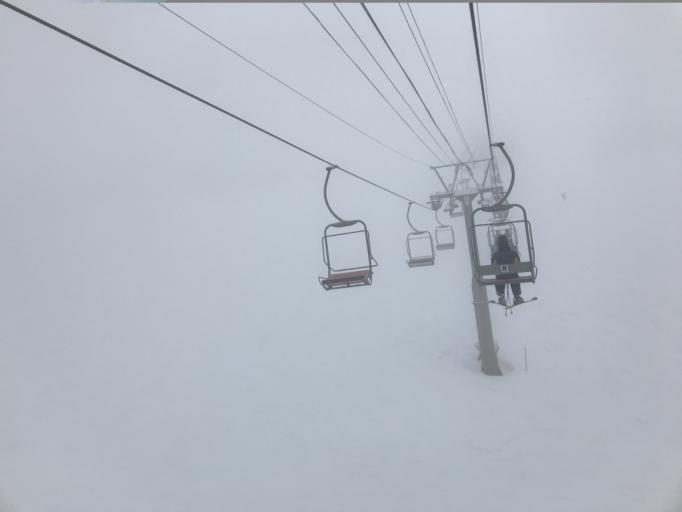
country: JP
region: Nagano
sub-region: Kitaazumi Gun
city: Hakuba
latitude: 36.7026
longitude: 137.8115
